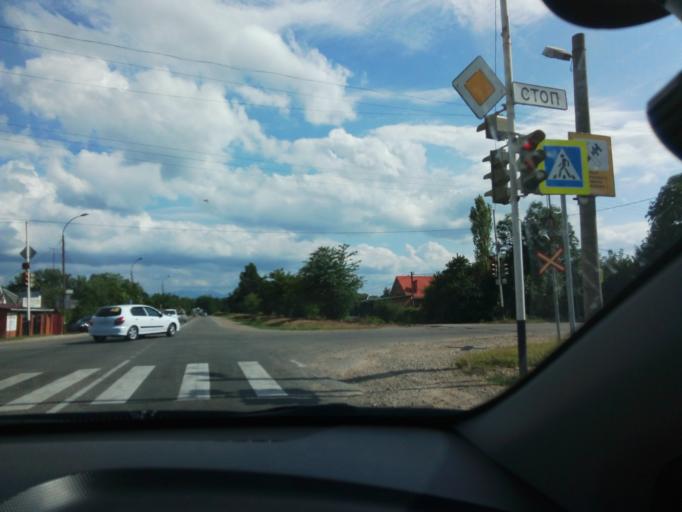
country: RU
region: Krasnodarskiy
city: Apsheronsk
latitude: 44.4601
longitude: 39.7300
